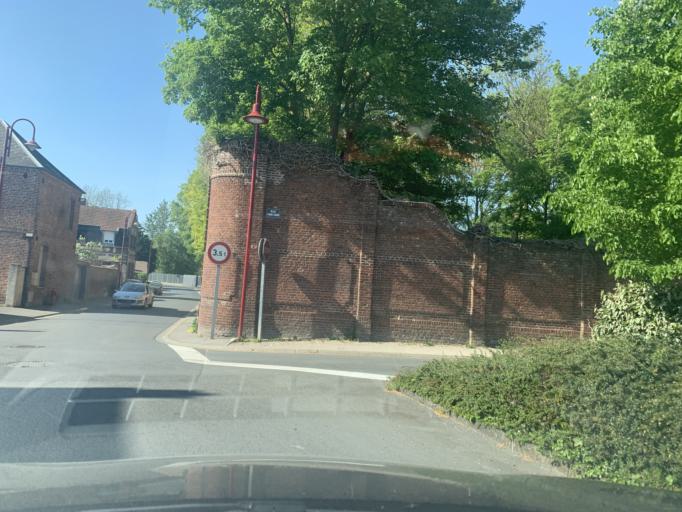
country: FR
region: Nord-Pas-de-Calais
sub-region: Departement du Nord
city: Proville
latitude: 50.1634
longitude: 3.2096
